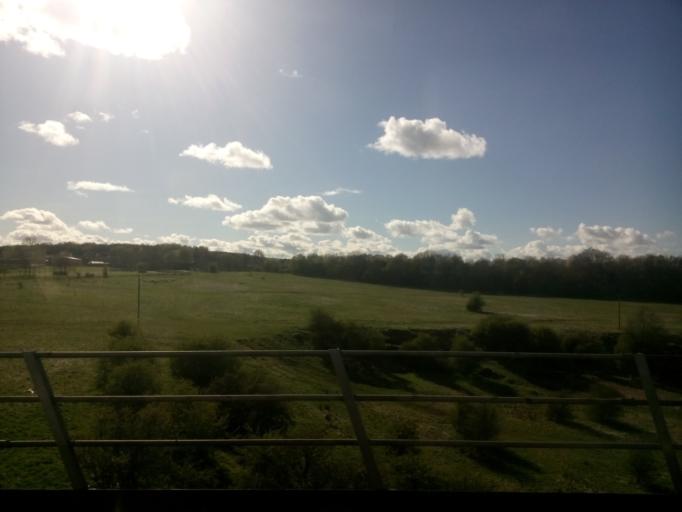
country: GB
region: England
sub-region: County Durham
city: Durham
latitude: 54.7626
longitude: -1.6071
